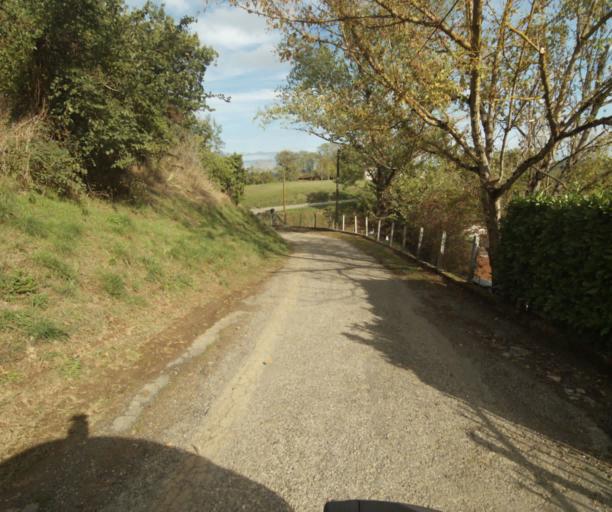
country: FR
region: Midi-Pyrenees
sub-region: Departement du Tarn-et-Garonne
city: Saint-Porquier
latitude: 43.9452
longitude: 1.1666
